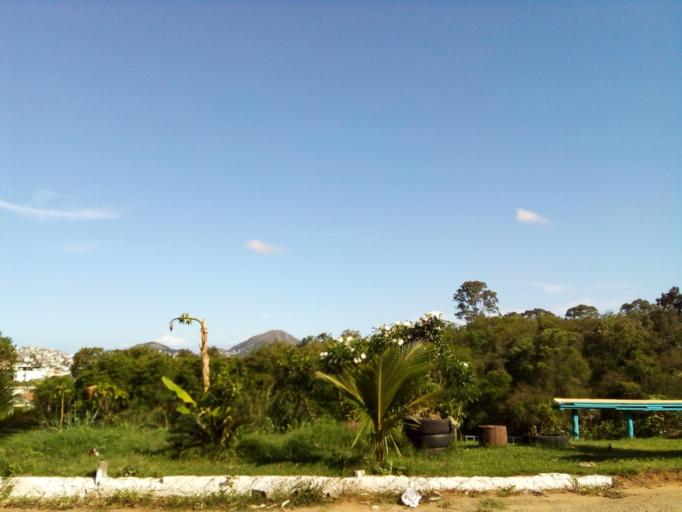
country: BR
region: Espirito Santo
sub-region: Vitoria
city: Vitoria
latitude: -20.3078
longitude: -40.3727
